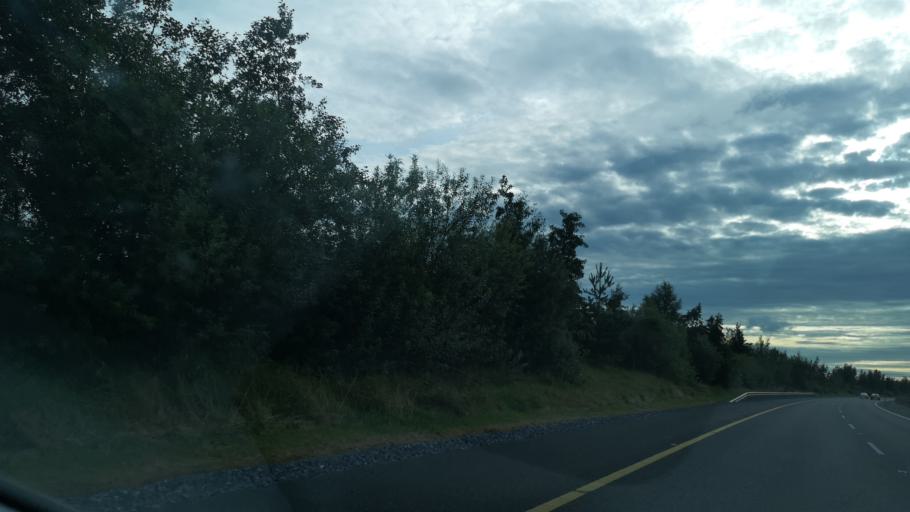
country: IE
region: Connaught
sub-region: County Galway
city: Ballinasloe
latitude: 53.3066
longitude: -8.2810
